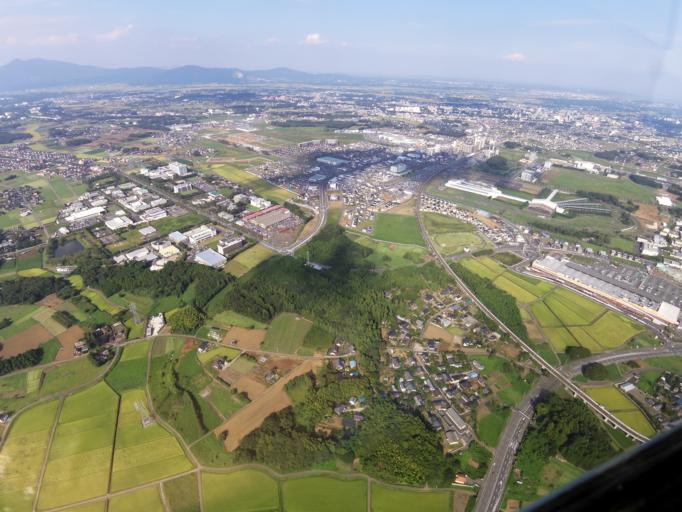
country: JP
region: Ibaraki
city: Mitsukaido
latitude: 36.0775
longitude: 140.0612
